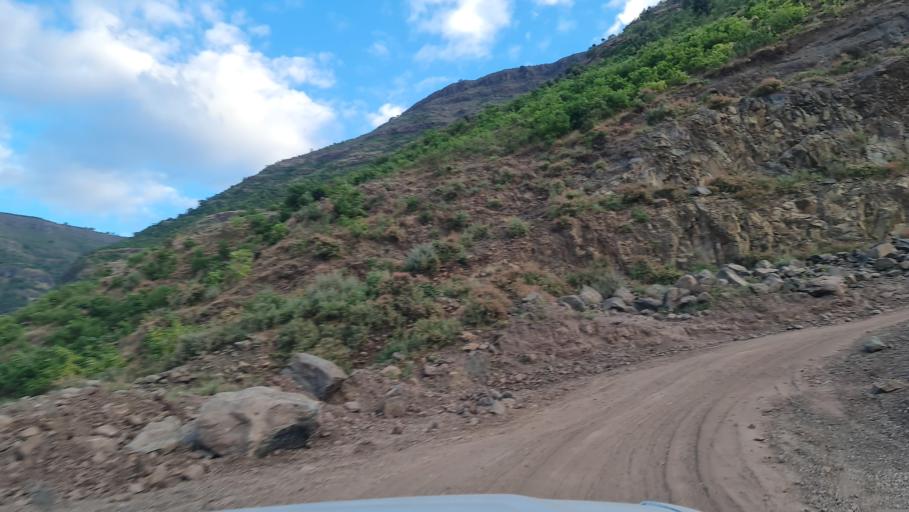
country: ET
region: Amhara
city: Debark'
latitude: 13.0147
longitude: 38.0550
